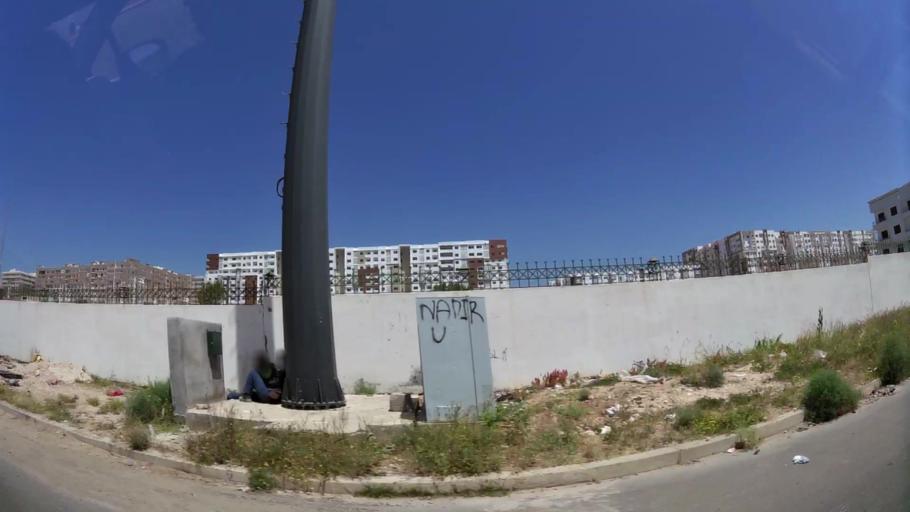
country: MA
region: Oued ed Dahab-Lagouira
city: Dakhla
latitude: 30.4331
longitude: -9.5632
